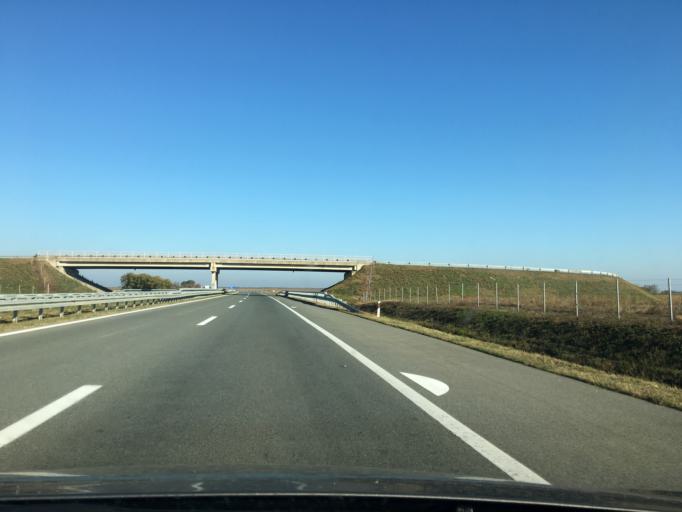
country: RS
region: Autonomna Pokrajina Vojvodina
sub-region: Severnobacki Okrug
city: Mali Igos
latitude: 45.6651
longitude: 19.7275
